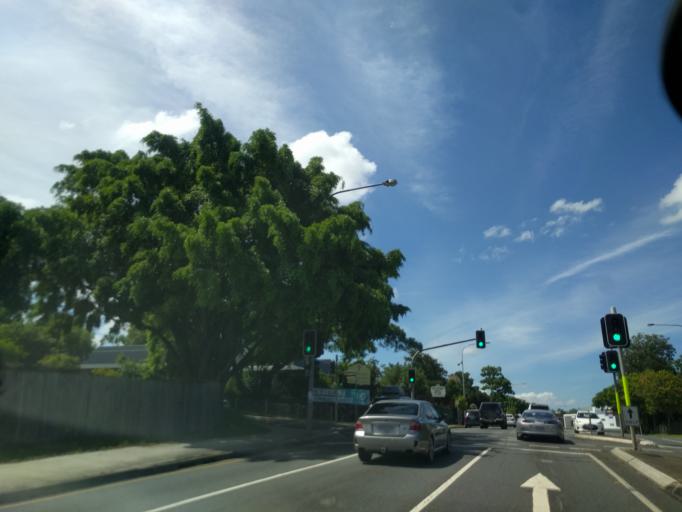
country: AU
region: Queensland
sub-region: Brisbane
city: Wilston
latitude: -27.4409
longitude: 153.0069
